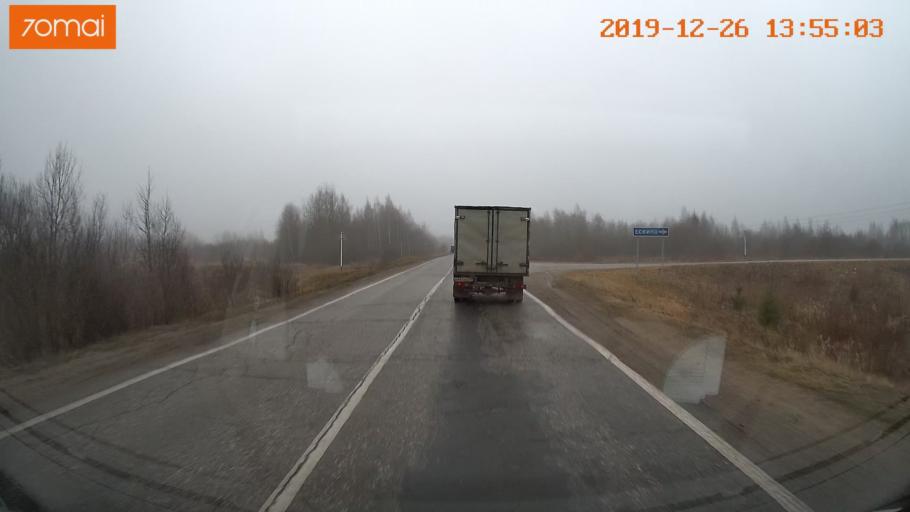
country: RU
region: Jaroslavl
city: Poshekhon'ye
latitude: 58.6074
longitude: 38.6427
